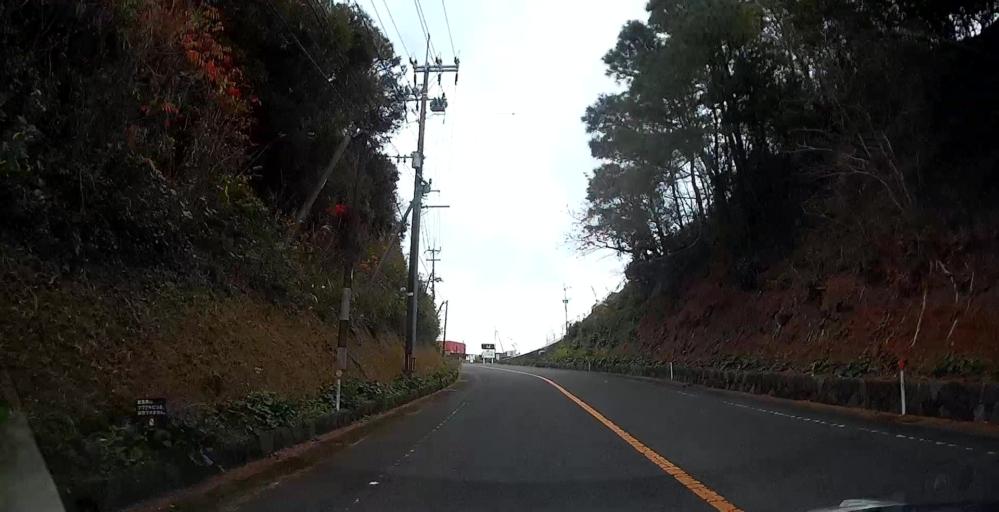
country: JP
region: Kagoshima
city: Akune
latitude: 32.1088
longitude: 130.1454
